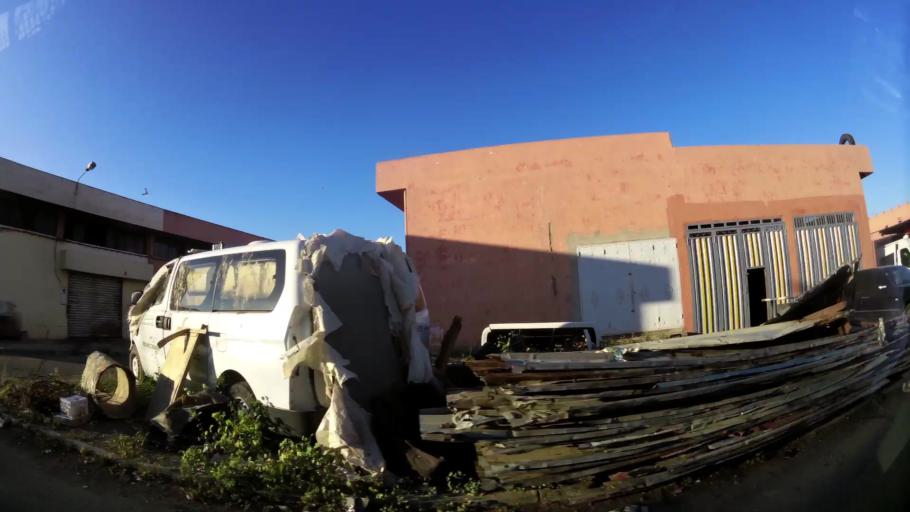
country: MA
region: Marrakech-Tensift-Al Haouz
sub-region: Kelaa-Des-Sraghna
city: Sidi Abdallah
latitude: 32.2383
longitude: -7.9644
